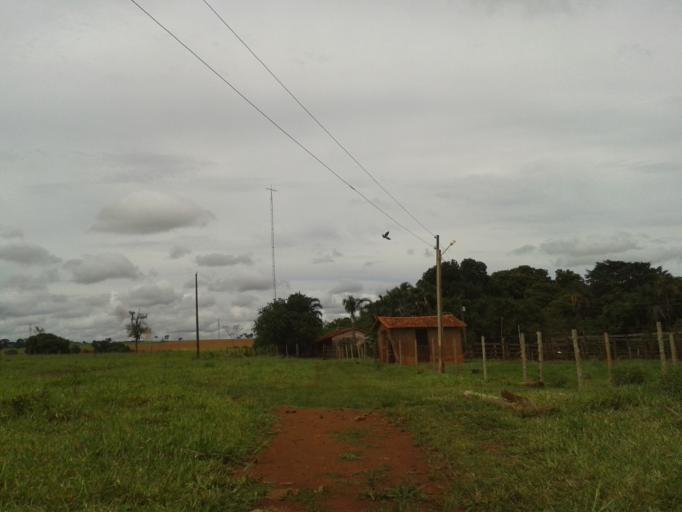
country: BR
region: Minas Gerais
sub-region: Capinopolis
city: Capinopolis
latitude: -18.7758
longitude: -49.7731
